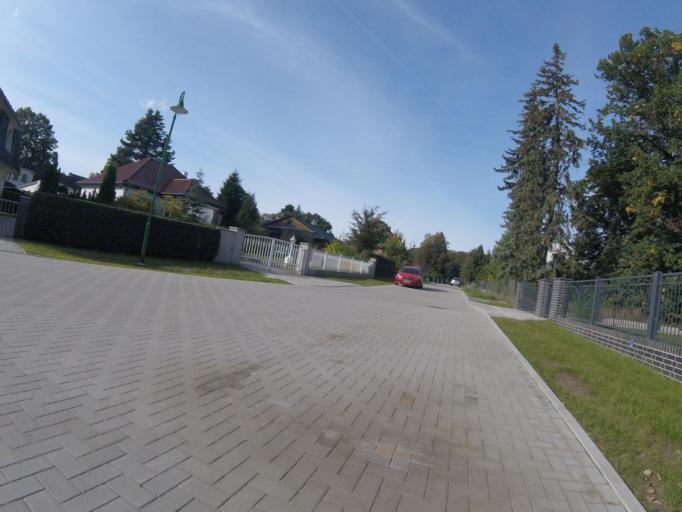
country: DE
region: Brandenburg
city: Konigs Wusterhausen
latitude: 52.2958
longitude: 13.6920
